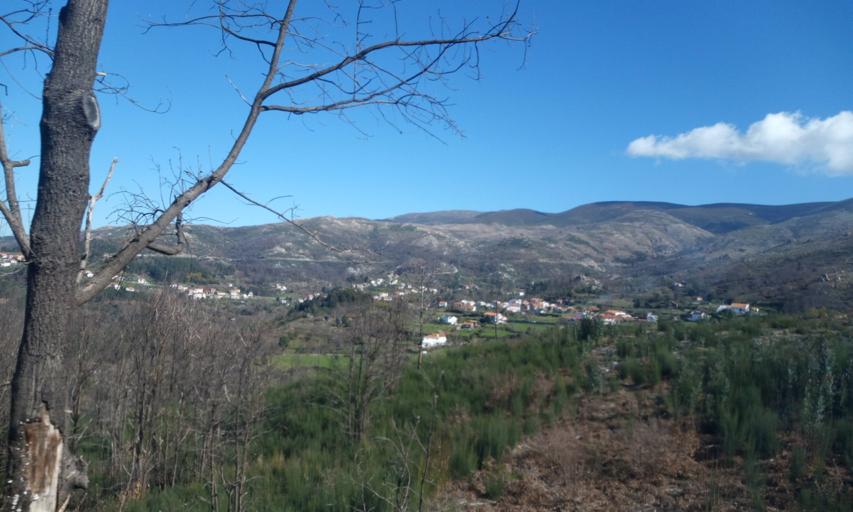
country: PT
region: Guarda
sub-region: Manteigas
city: Manteigas
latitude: 40.4658
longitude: -7.6137
